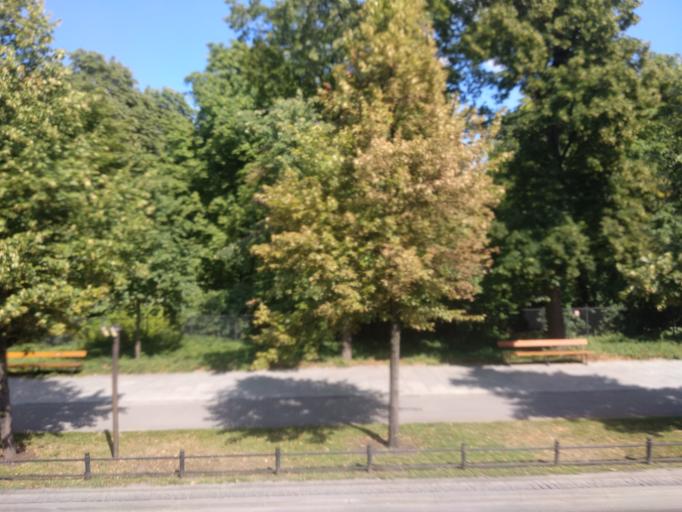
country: PL
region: Masovian Voivodeship
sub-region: Warszawa
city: Srodmiescie
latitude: 52.2206
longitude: 21.0248
